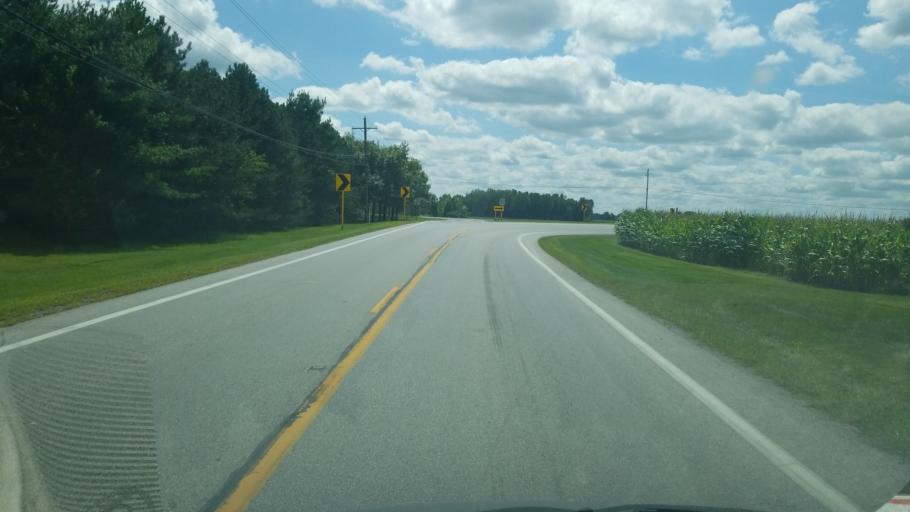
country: US
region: Ohio
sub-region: Fulton County
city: Delta
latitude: 41.5171
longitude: -84.0038
